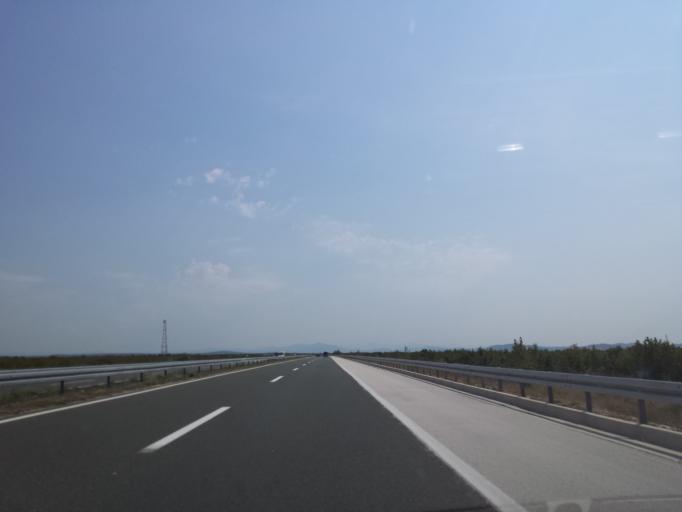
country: HR
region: Sibensko-Kniniska
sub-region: Grad Sibenik
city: Pirovac
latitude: 43.9148
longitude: 15.7468
